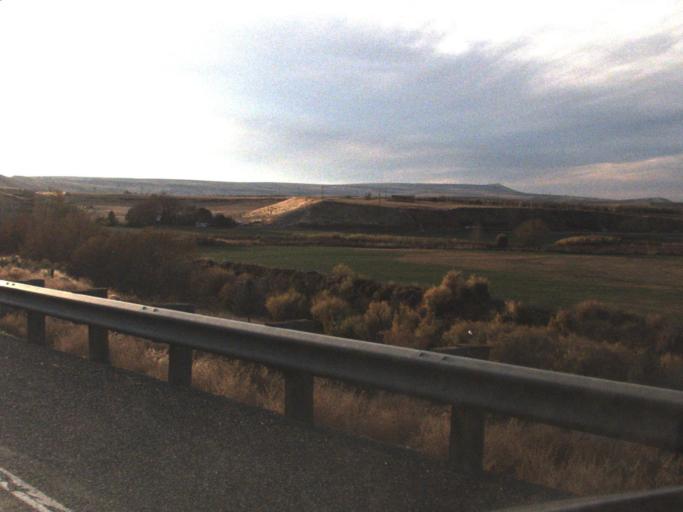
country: US
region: Washington
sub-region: Benton County
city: Finley
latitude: 46.0689
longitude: -118.8201
